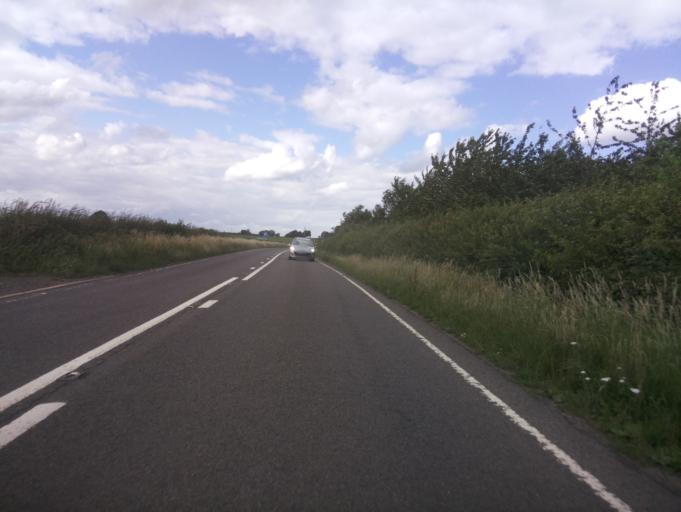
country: GB
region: England
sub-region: Leicestershire
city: Market Bosworth
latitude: 52.6099
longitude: -1.4760
